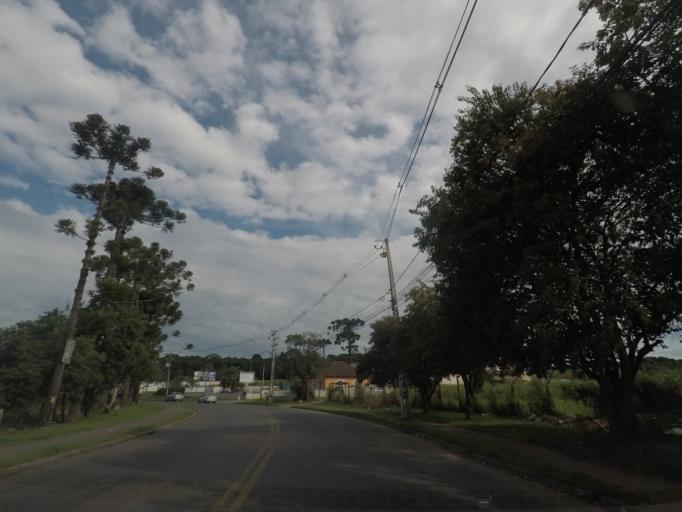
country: BR
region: Parana
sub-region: Sao Jose Dos Pinhais
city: Sao Jose dos Pinhais
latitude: -25.5544
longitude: -49.2940
